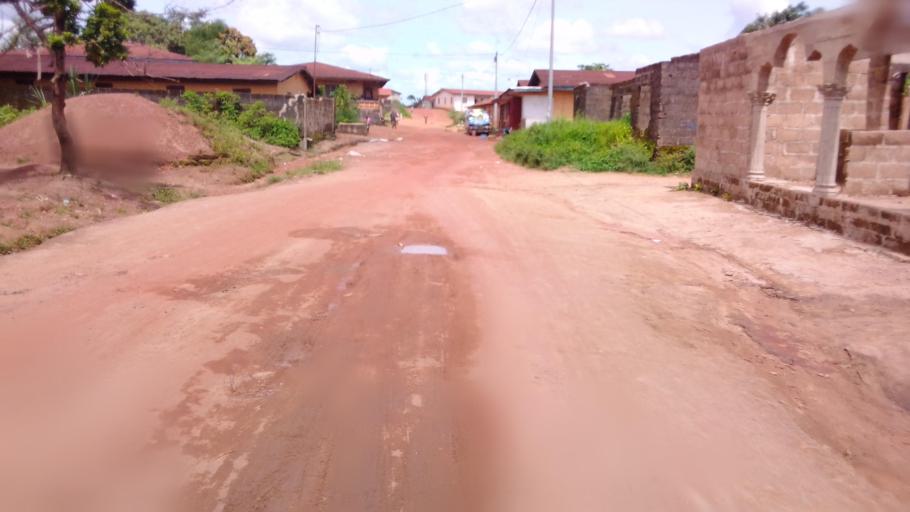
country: SL
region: Northern Province
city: Makeni
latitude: 8.8857
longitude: -12.0361
